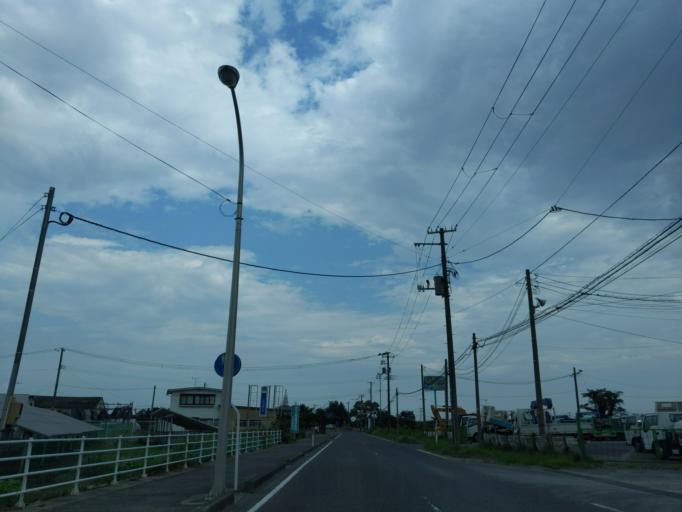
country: JP
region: Miyagi
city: Tomiya
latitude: 38.4325
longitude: 140.8878
